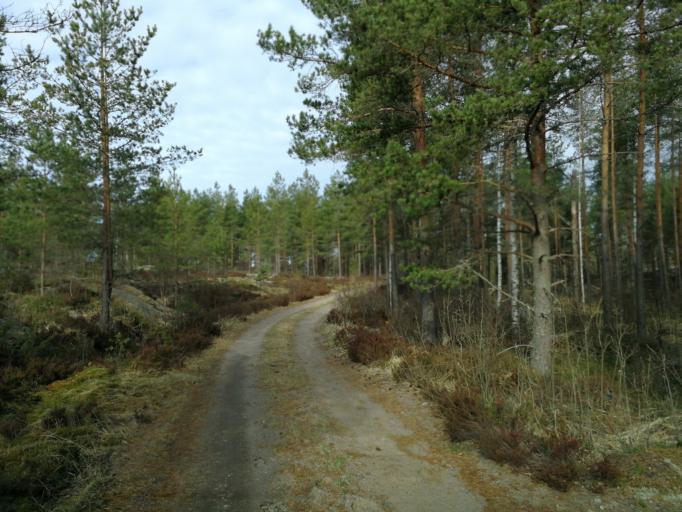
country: FI
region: Uusimaa
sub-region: Helsinki
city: Karjalohja
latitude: 60.2127
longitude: 23.6623
